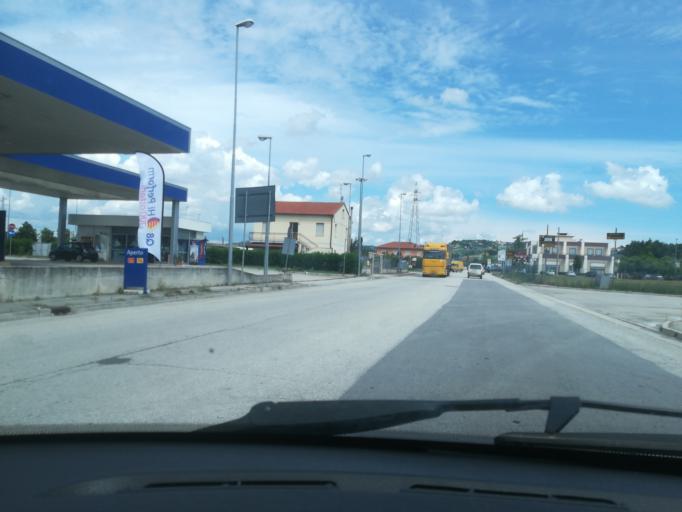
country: IT
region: The Marches
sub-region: Provincia di Macerata
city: Santa Maria Apparente
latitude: 43.2826
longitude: 13.6843
